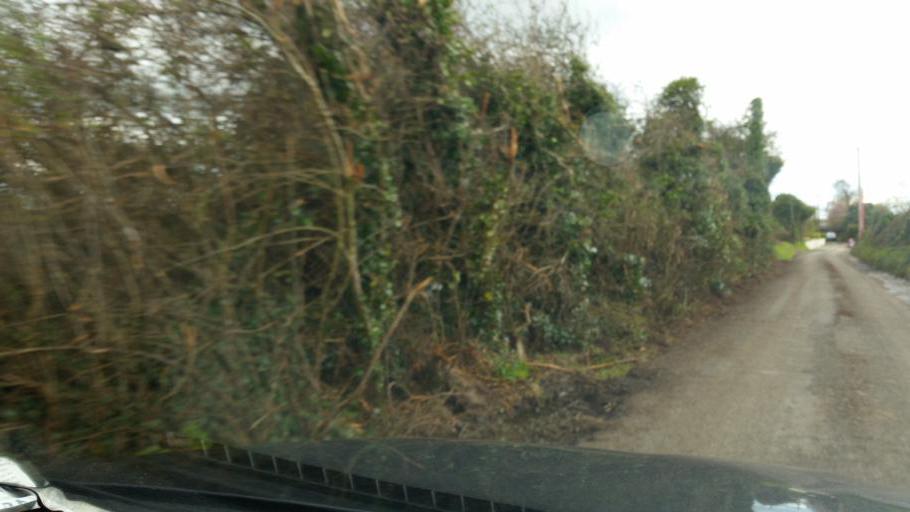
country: IE
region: Leinster
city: Kinsealy-Drinan
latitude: 53.4427
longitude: -6.2202
